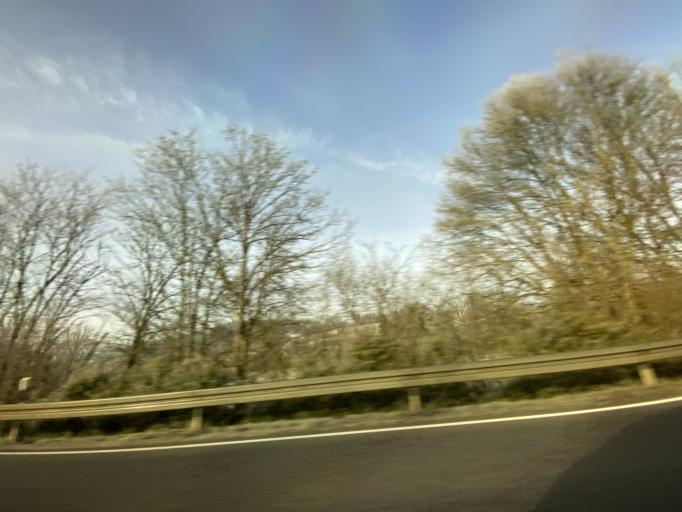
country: DE
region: Hesse
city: Staufenberg
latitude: 50.7168
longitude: 8.7800
